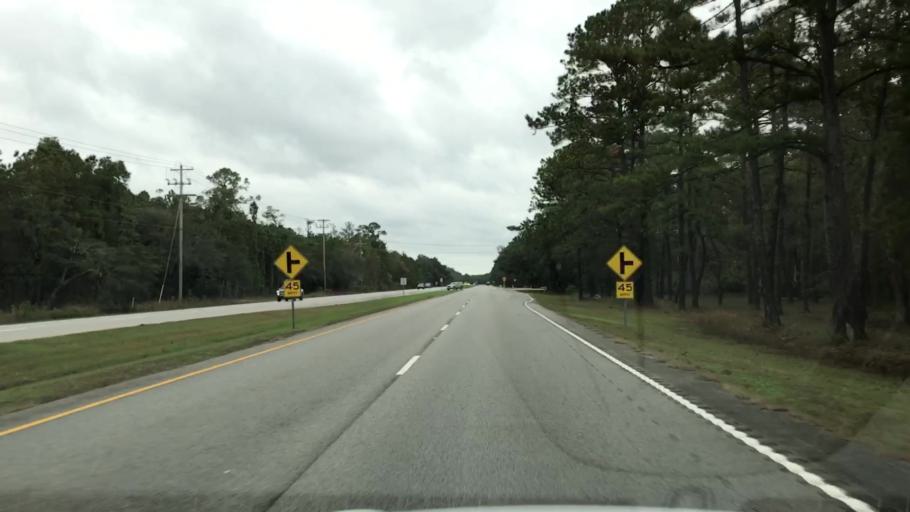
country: US
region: South Carolina
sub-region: Georgetown County
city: Georgetown
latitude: 33.3740
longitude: -79.2151
